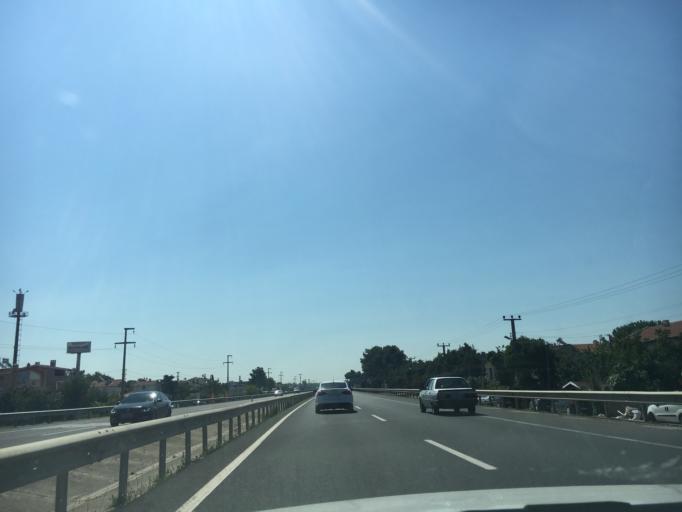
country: TR
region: Tekirdag
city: Marmara Ereglisi
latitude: 40.9925
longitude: 27.8451
